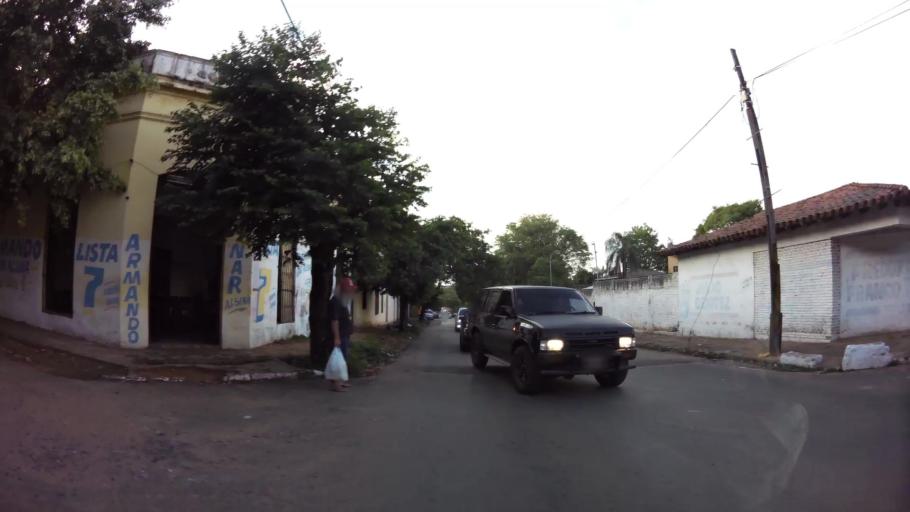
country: PY
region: Central
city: San Lorenzo
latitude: -25.3405
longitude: -57.5061
